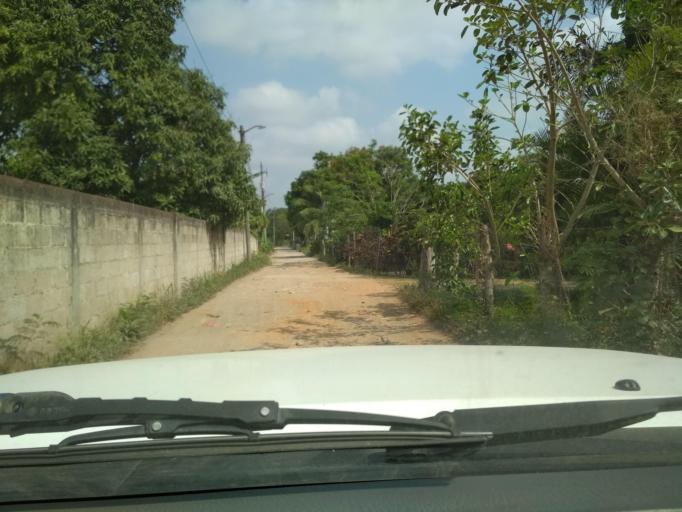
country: MX
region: Veracruz
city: El Tejar
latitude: 19.0772
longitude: -96.1700
